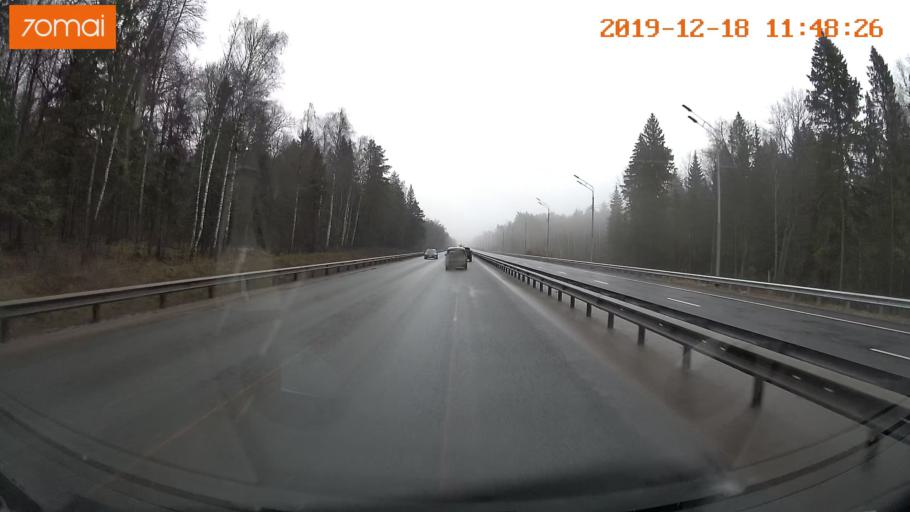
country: RU
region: Moskovskaya
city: Yershovo
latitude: 55.7681
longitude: 36.9035
